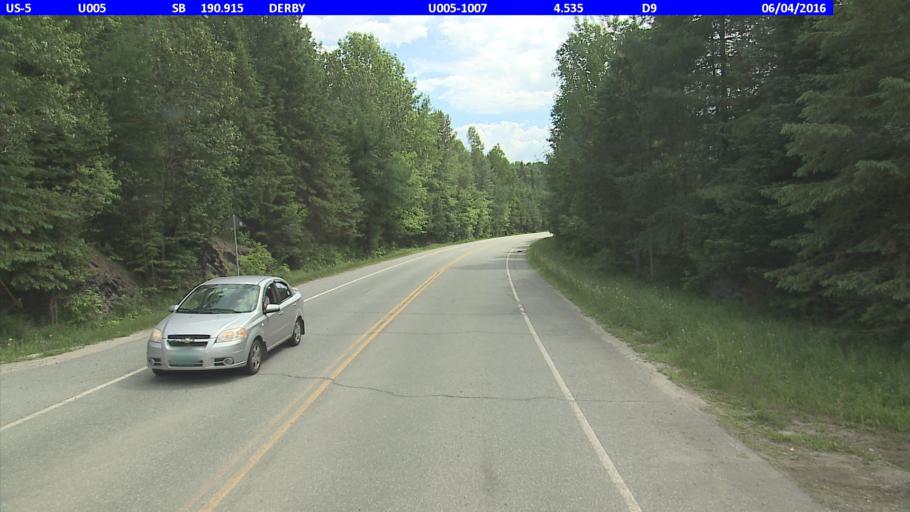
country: US
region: Vermont
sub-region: Orleans County
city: Newport
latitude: 44.9865
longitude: -72.1066
